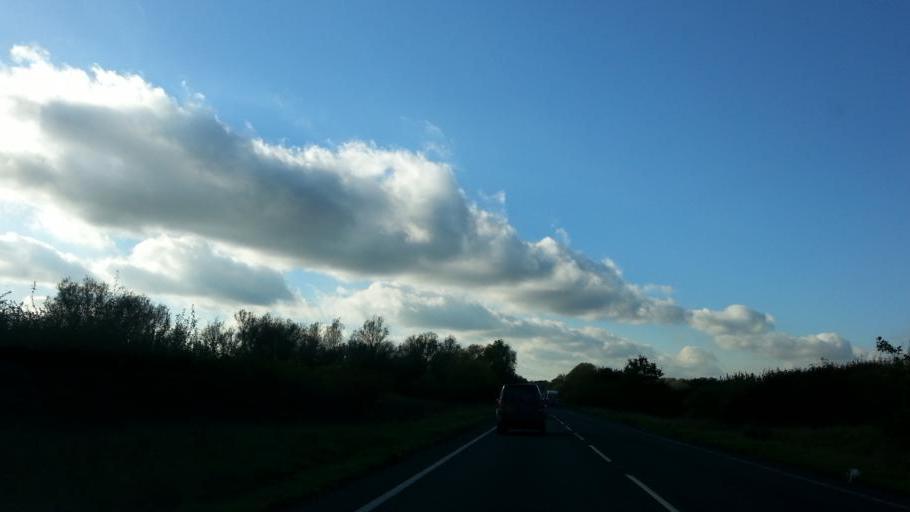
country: GB
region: England
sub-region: Norfolk
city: Diss
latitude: 52.3629
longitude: 1.1652
